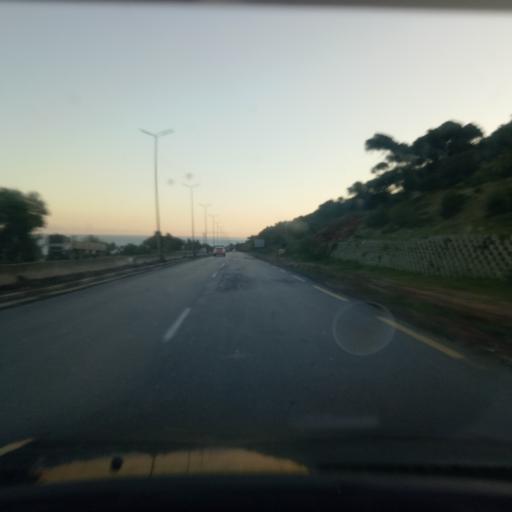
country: DZ
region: Tipaza
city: Bou Ismail
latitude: 36.6525
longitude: 2.7157
